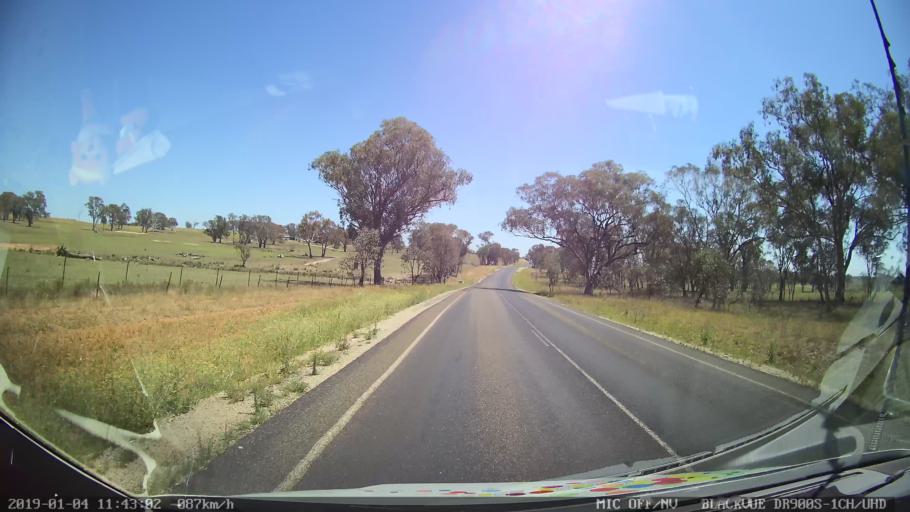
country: AU
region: New South Wales
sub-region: Cabonne
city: Molong
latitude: -32.9741
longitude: 148.7847
